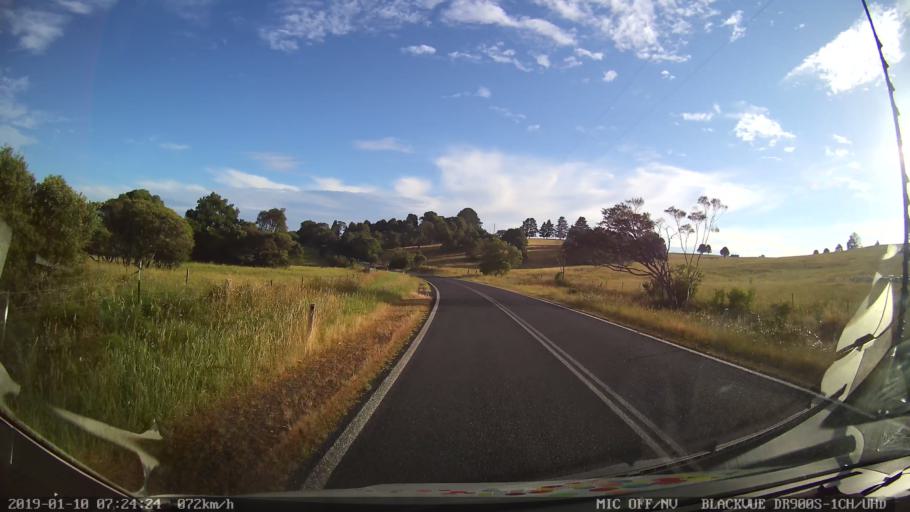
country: AU
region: New South Wales
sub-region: Bellingen
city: Dorrigo
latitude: -30.3761
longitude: 152.5814
